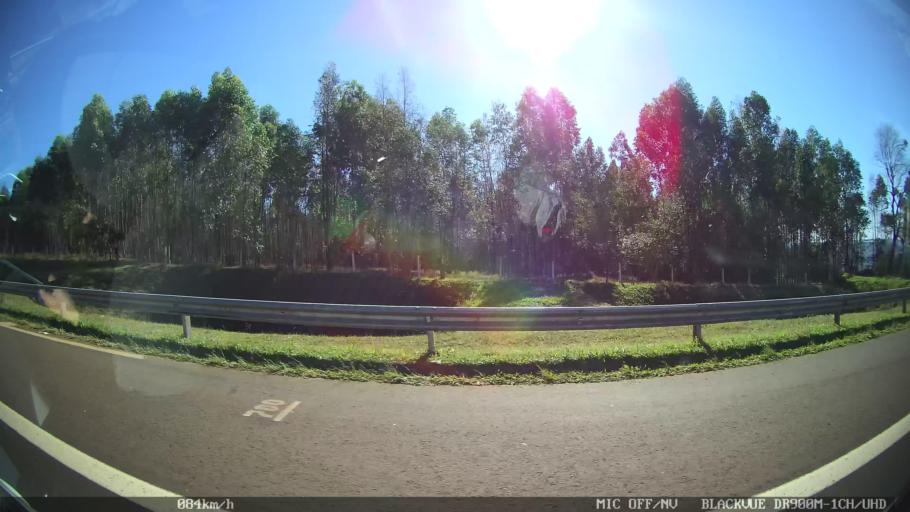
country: BR
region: Sao Paulo
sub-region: Franca
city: Franca
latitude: -20.5785
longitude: -47.3432
